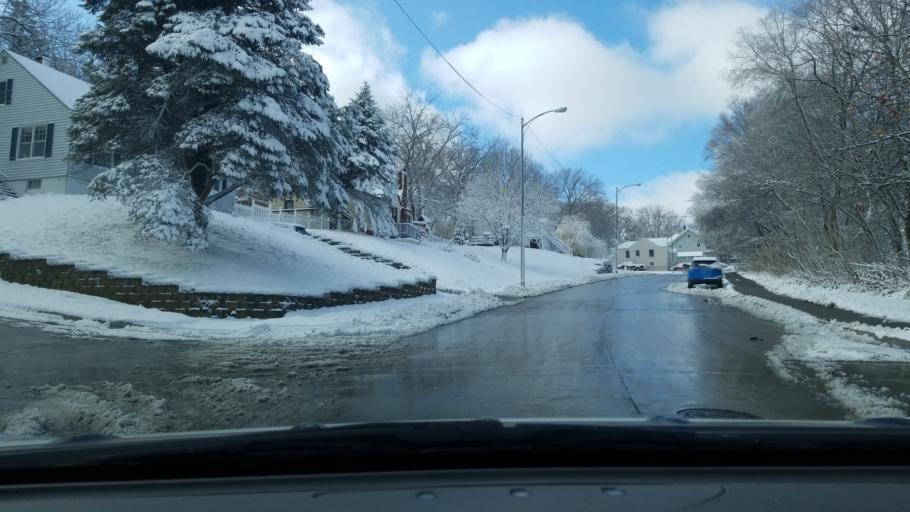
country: US
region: Nebraska
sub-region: Douglas County
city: Omaha
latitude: 41.2196
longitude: -95.9404
